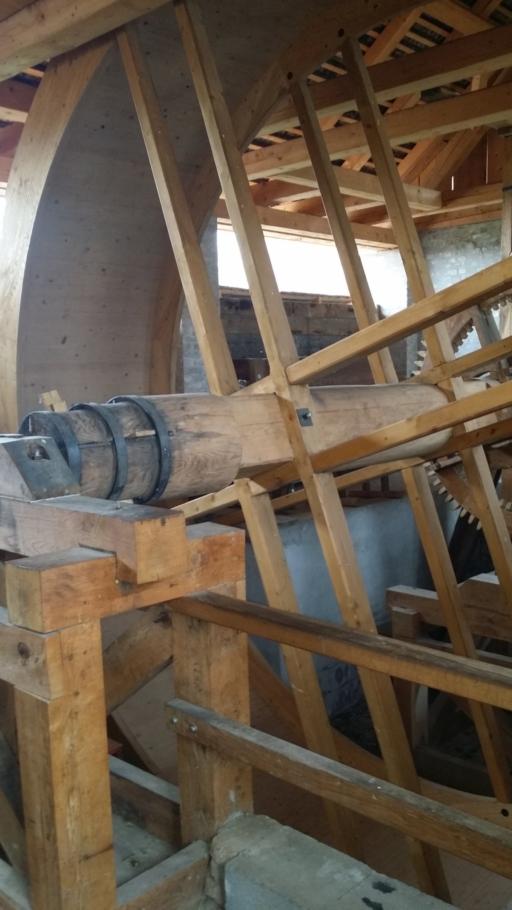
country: HU
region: Baranya
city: Mohacs
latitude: 46.0406
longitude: 18.6773
